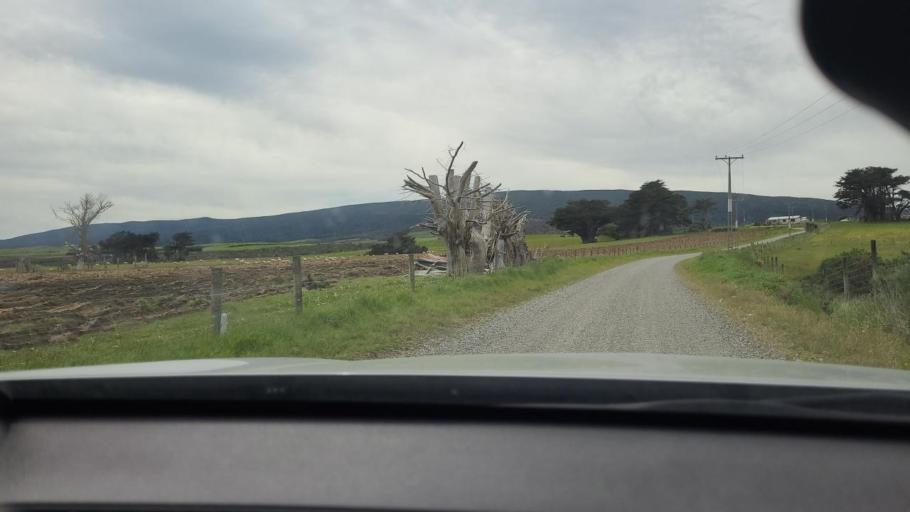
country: NZ
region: Southland
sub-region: Southland District
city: Riverton
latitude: -46.2803
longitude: 167.7506
